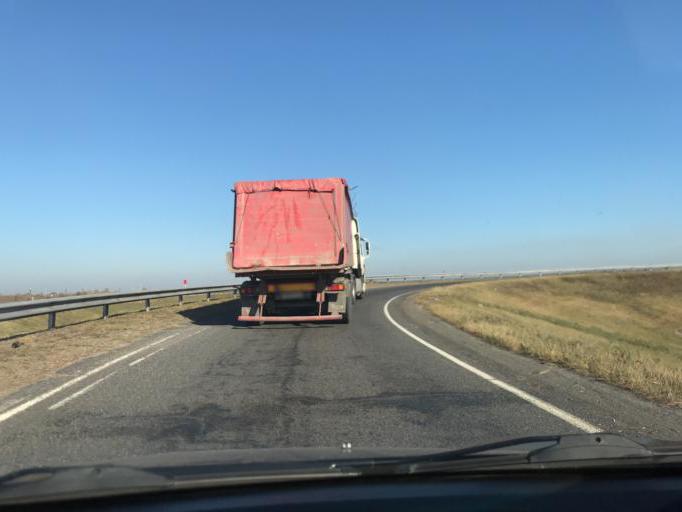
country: BY
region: Gomel
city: Horad Rechytsa
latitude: 52.2924
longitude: 30.4640
